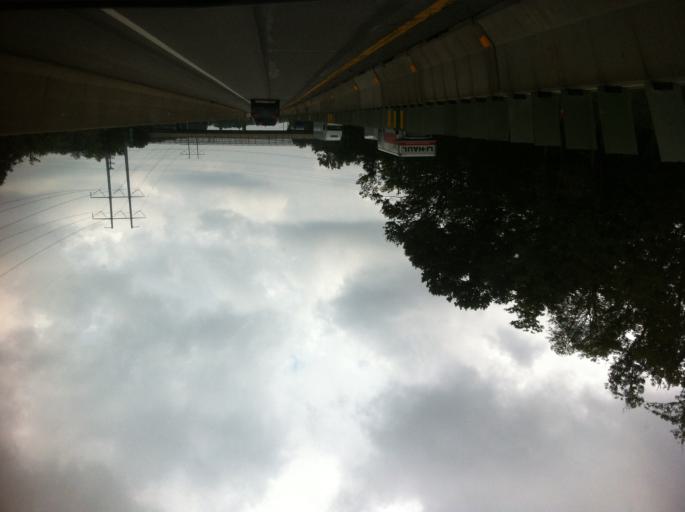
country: US
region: Ohio
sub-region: Cuyahoga County
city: Middleburg Heights
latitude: 41.3221
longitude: -81.7831
